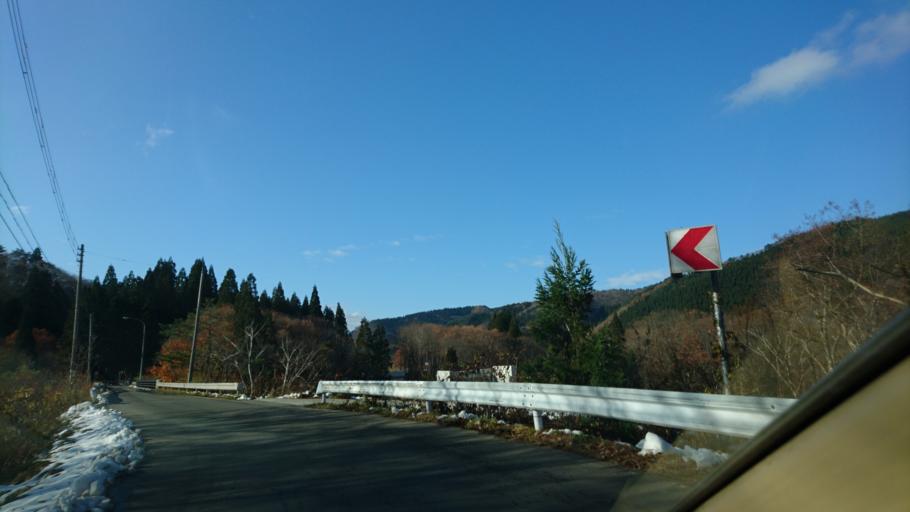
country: JP
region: Akita
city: Yokotemachi
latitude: 39.2984
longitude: 140.8311
